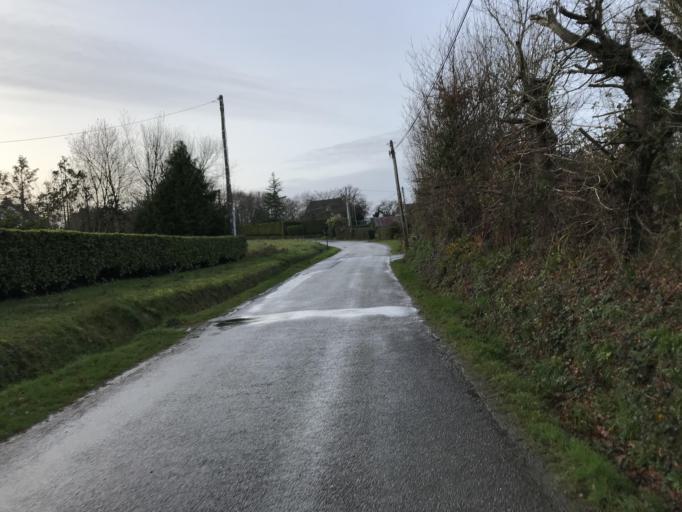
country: FR
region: Brittany
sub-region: Departement du Finistere
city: Logonna-Daoulas
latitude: 48.3248
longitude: -4.3070
